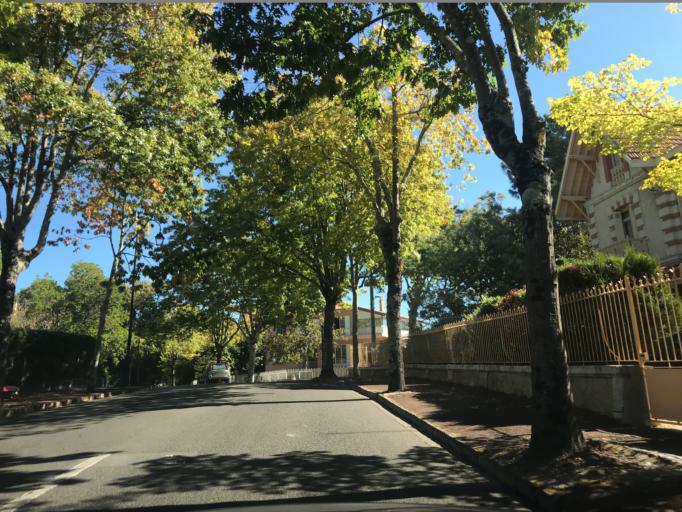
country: FR
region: Aquitaine
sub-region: Departement de la Gironde
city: Arcachon
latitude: 44.6565
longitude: -1.1723
